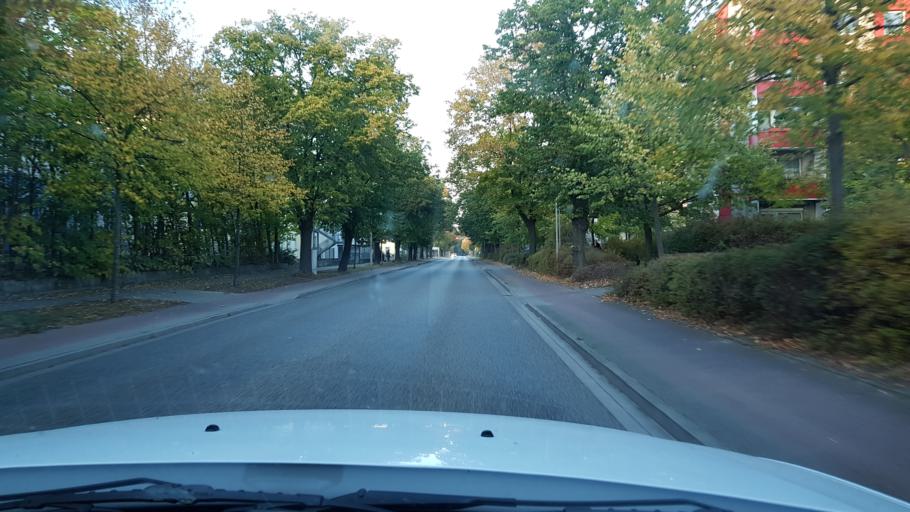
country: DE
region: Brandenburg
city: Schwedt (Oder)
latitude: 53.0662
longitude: 14.2980
